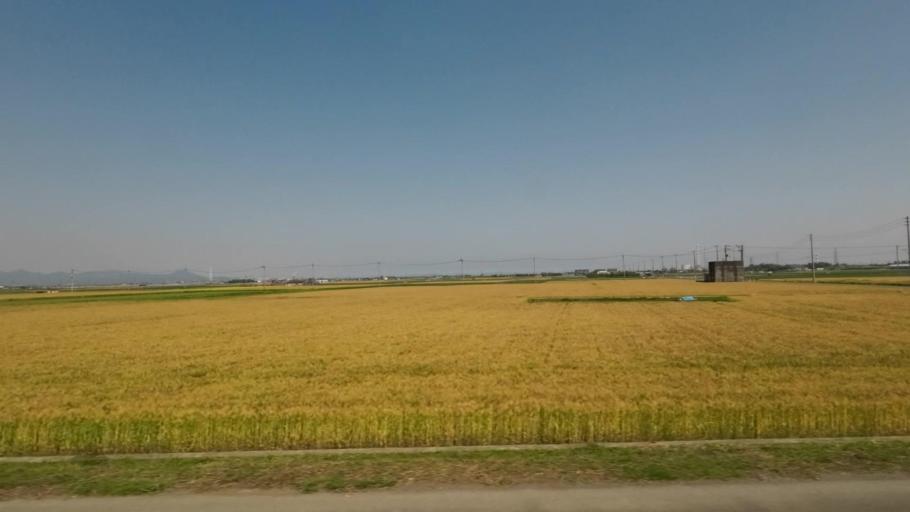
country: JP
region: Ehime
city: Saijo
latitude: 33.8976
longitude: 133.1667
